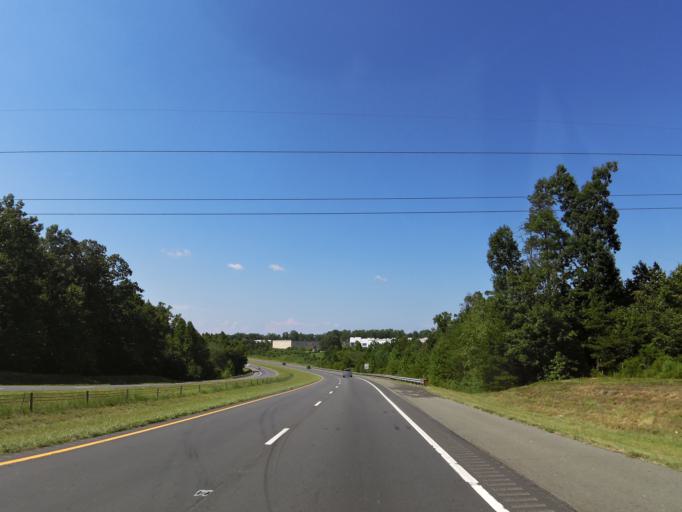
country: US
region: North Carolina
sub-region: Catawba County
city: Maiden
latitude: 35.5359
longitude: -81.2259
